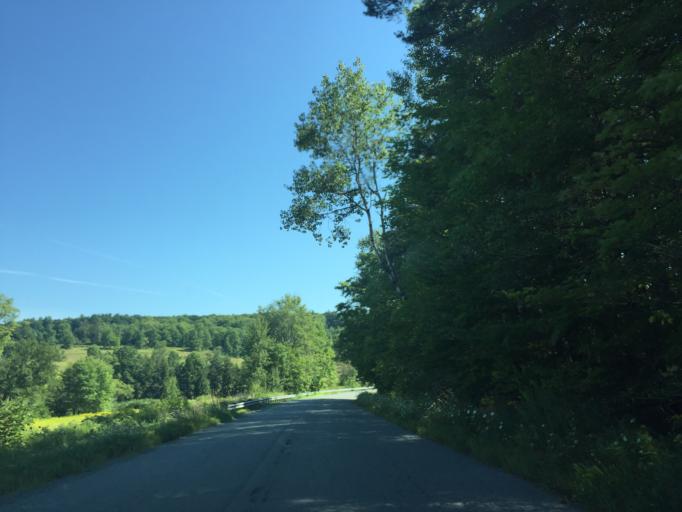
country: US
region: Pennsylvania
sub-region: Wayne County
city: Honesdale
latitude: 41.7650
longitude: -75.1201
